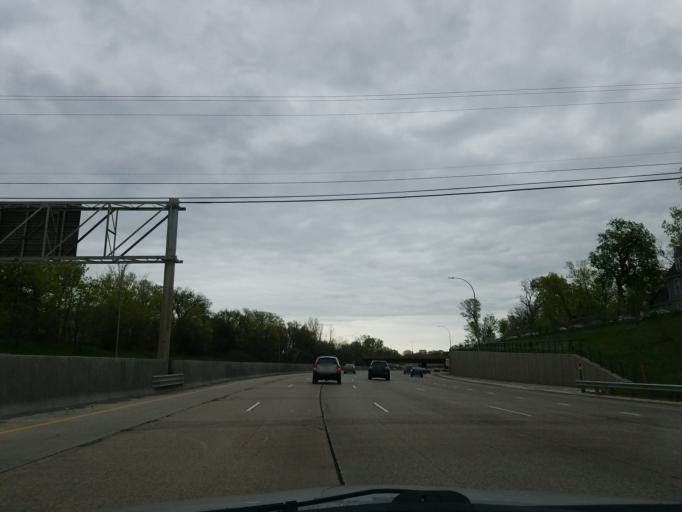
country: US
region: Minnesota
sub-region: Hennepin County
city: Minneapolis
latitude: 44.9847
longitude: -93.2415
